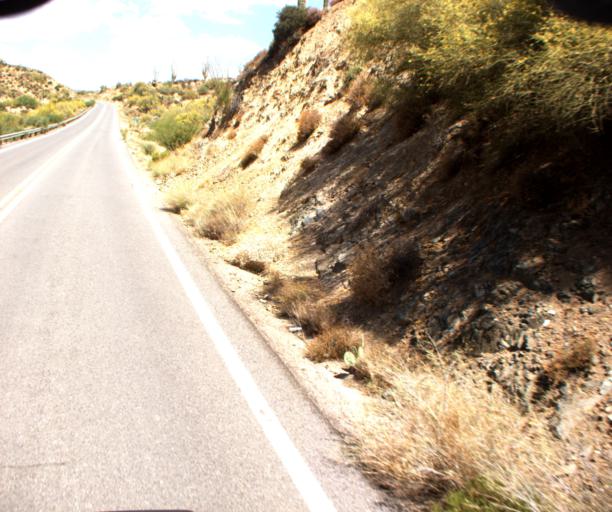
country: US
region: Arizona
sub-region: Pinal County
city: Superior
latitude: 33.1765
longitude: -111.0360
